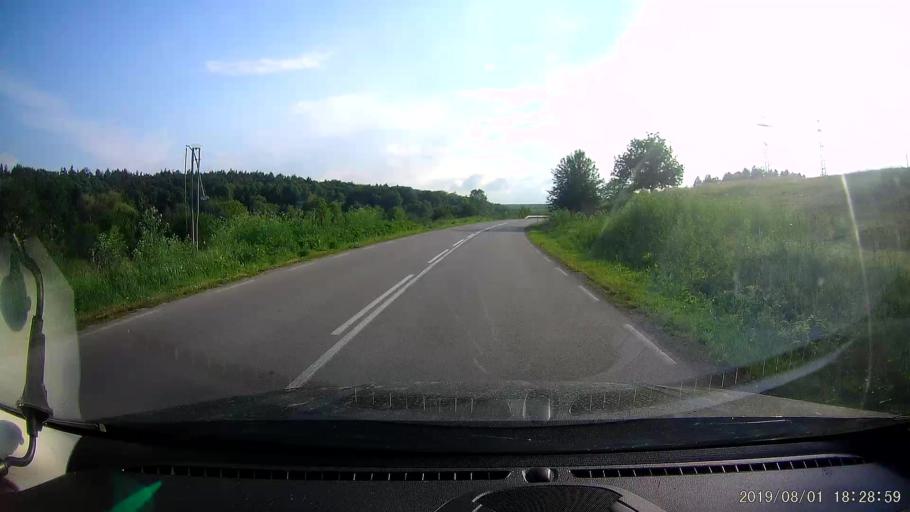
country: BG
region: Shumen
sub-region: Obshtina Venets
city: Venets
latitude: 43.5679
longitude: 26.9515
